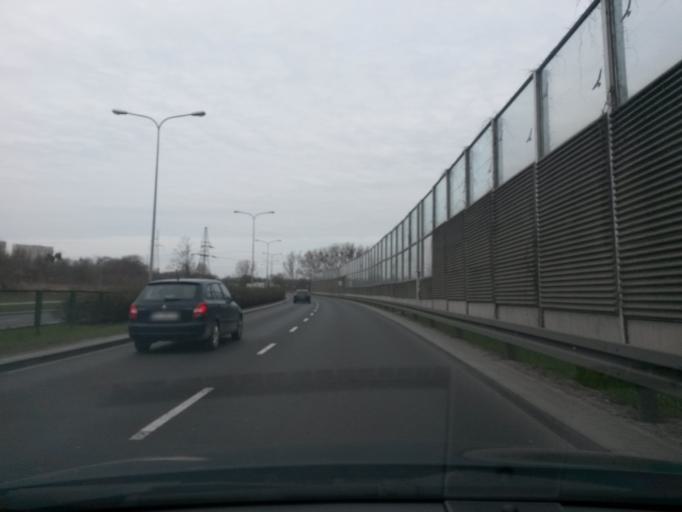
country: PL
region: Greater Poland Voivodeship
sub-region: Poznan
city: Poznan
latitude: 52.4390
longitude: 16.9517
